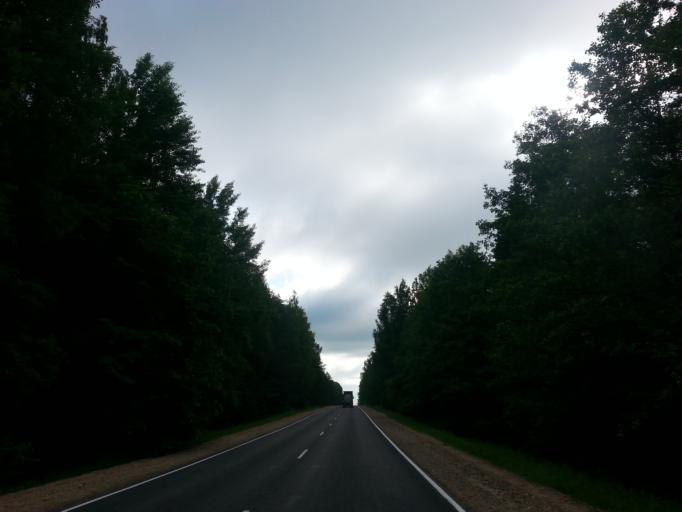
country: BY
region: Minsk
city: Myadzyel
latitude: 55.0514
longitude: 27.0996
